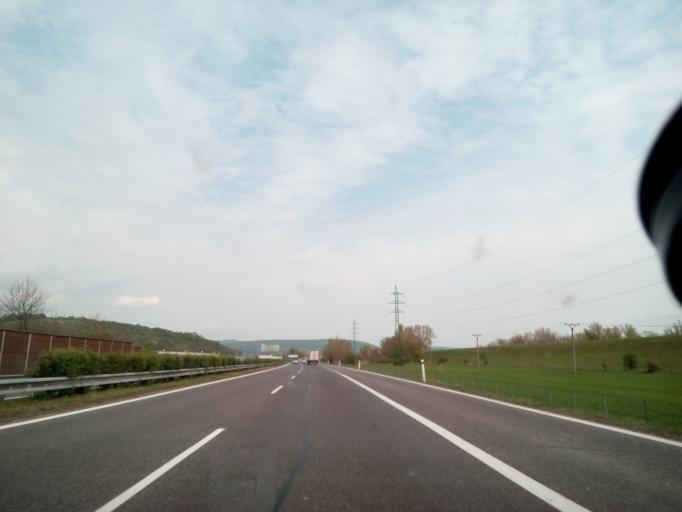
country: SK
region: Trenciansky
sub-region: Okres Trencin
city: Trencin
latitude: 48.8700
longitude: 17.9700
